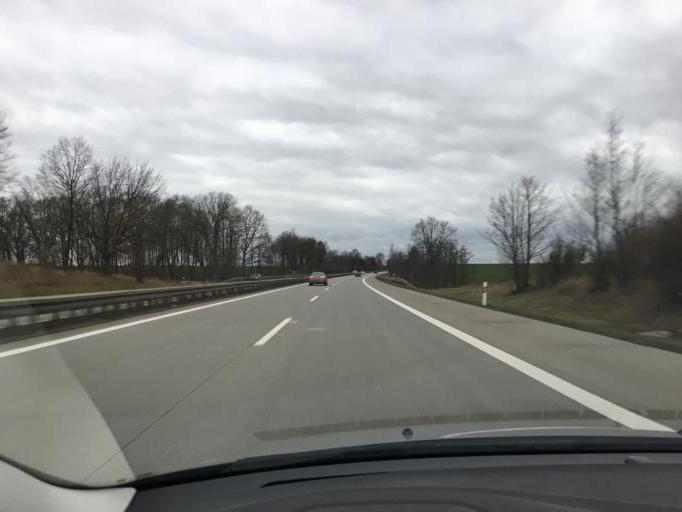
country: DE
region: Saxony
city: Nossen
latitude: 51.0725
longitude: 13.3148
